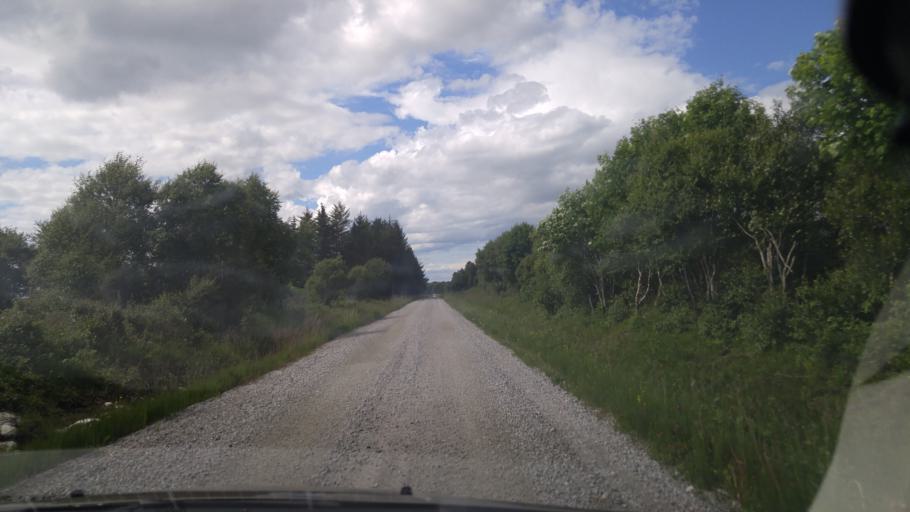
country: NO
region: Nord-Trondelag
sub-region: Vikna
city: Rorvik
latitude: 64.9068
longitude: 11.1318
